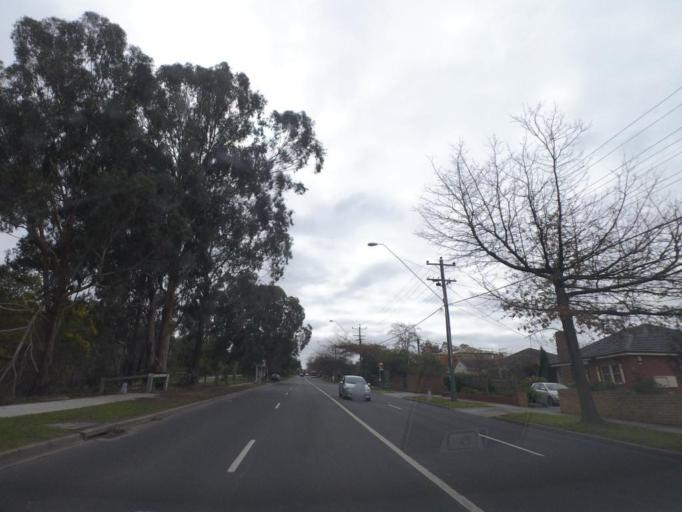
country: AU
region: Victoria
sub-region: Whitehorse
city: Burwood
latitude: -37.8422
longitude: 145.1104
